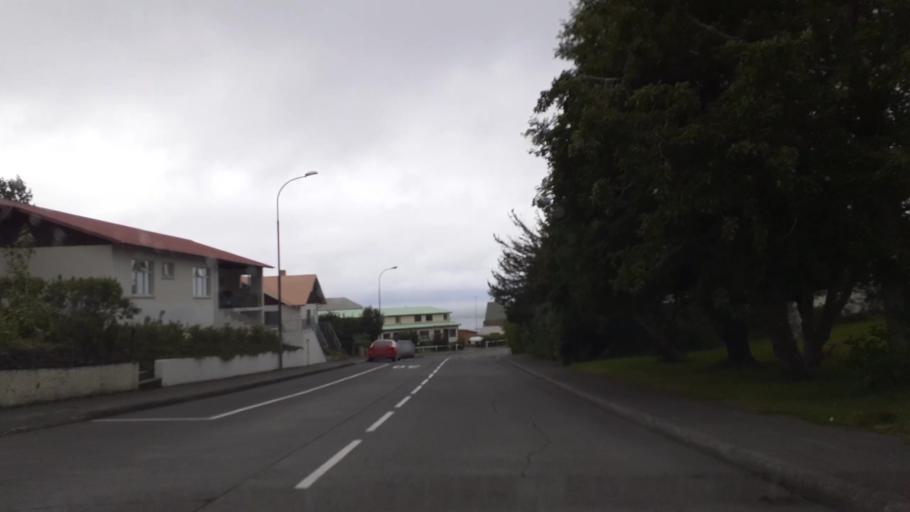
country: IS
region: Northeast
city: Husavik
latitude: 66.0405
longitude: -17.3379
